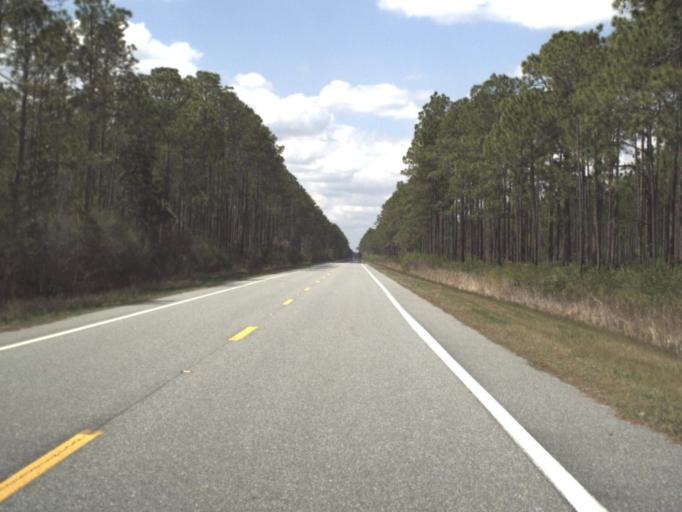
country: US
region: Florida
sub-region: Franklin County
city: Eastpoint
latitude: 29.8376
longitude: -84.9336
